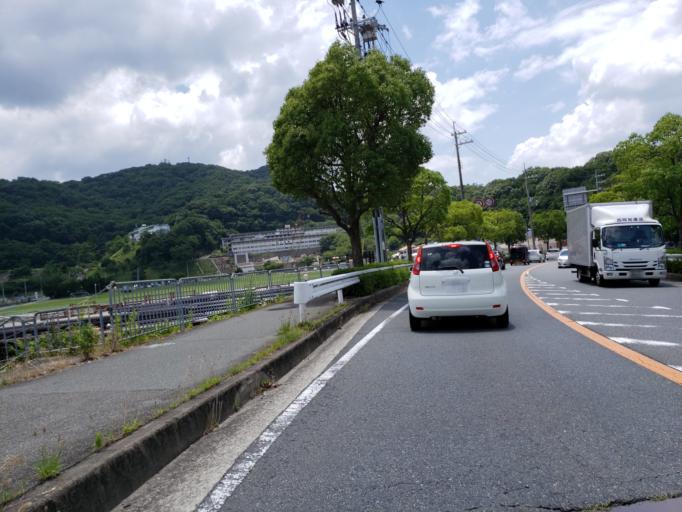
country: JP
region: Hyogo
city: Aioi
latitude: 34.8033
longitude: 134.4589
